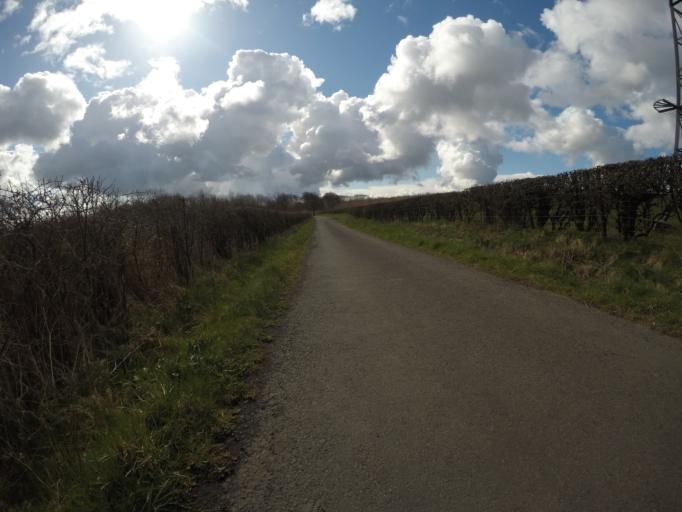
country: GB
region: Scotland
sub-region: North Ayrshire
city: Kilbirnie
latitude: 55.7298
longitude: -4.6700
